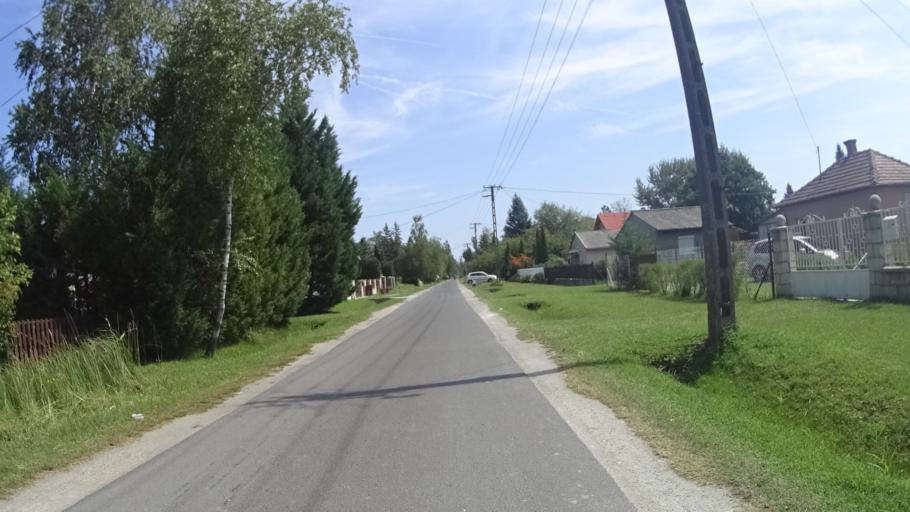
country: HU
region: Somogy
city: Balatonfenyves
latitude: 46.7076
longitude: 17.4451
